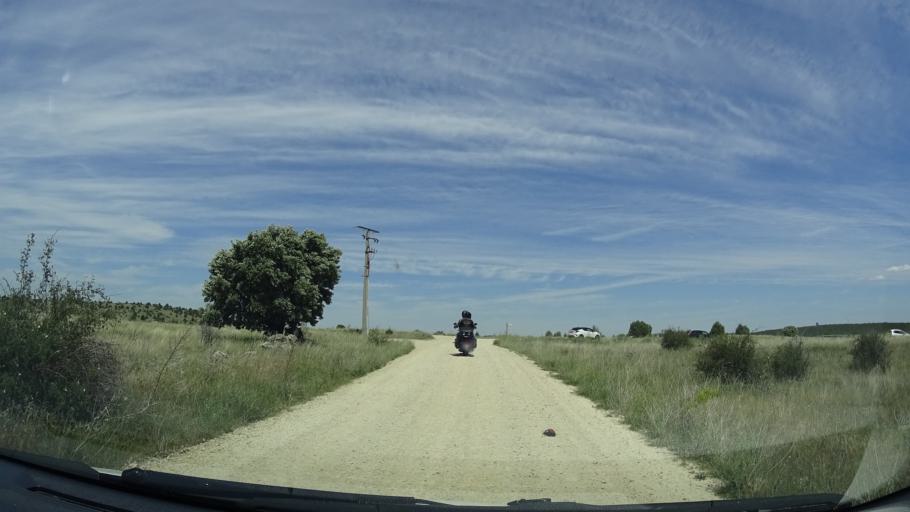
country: ES
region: Castille and Leon
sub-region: Provincia de Segovia
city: Pradena
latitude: 41.1450
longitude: -3.6787
